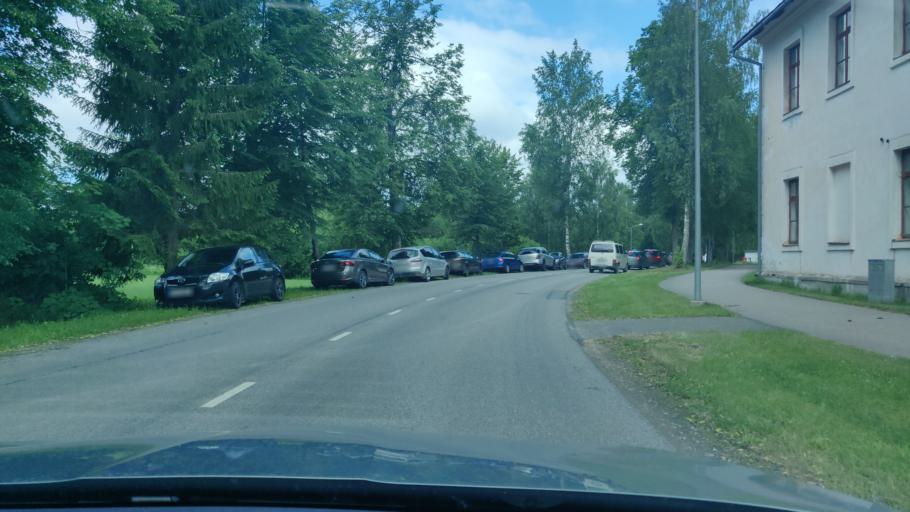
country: EE
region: Vorumaa
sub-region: Voru linn
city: Voru
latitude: 57.7295
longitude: 27.2920
